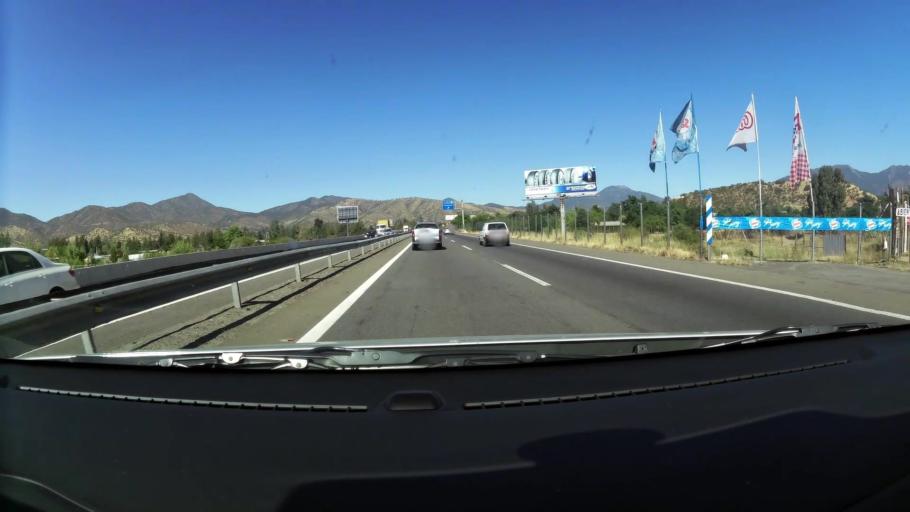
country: CL
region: Santiago Metropolitan
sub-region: Provincia de Melipilla
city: Melipilla
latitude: -33.4117
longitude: -71.1460
